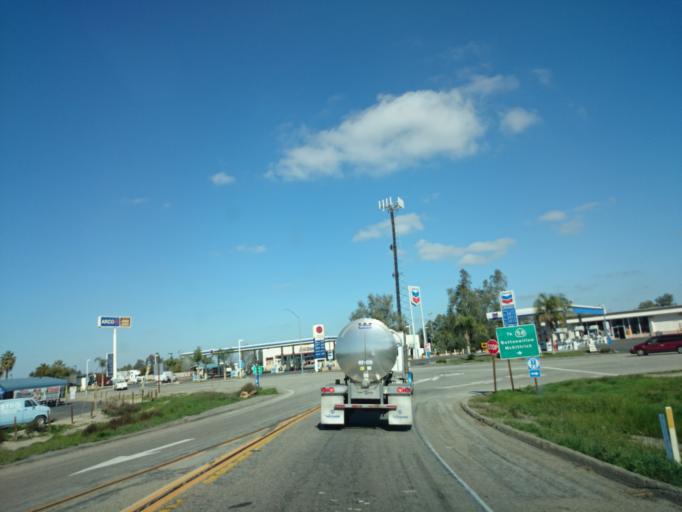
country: US
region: California
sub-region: Kern County
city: Buttonwillow
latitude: 35.4013
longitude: -119.3989
